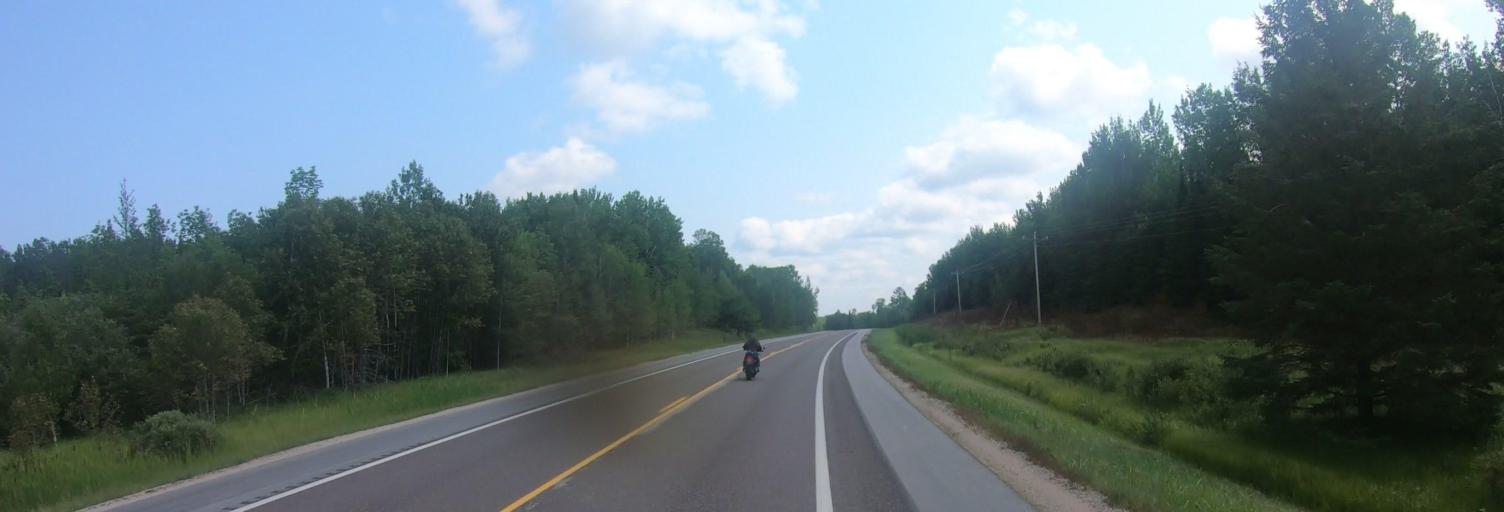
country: US
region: Minnesota
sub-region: Saint Louis County
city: Mountain Iron
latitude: 48.0546
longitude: -92.7800
